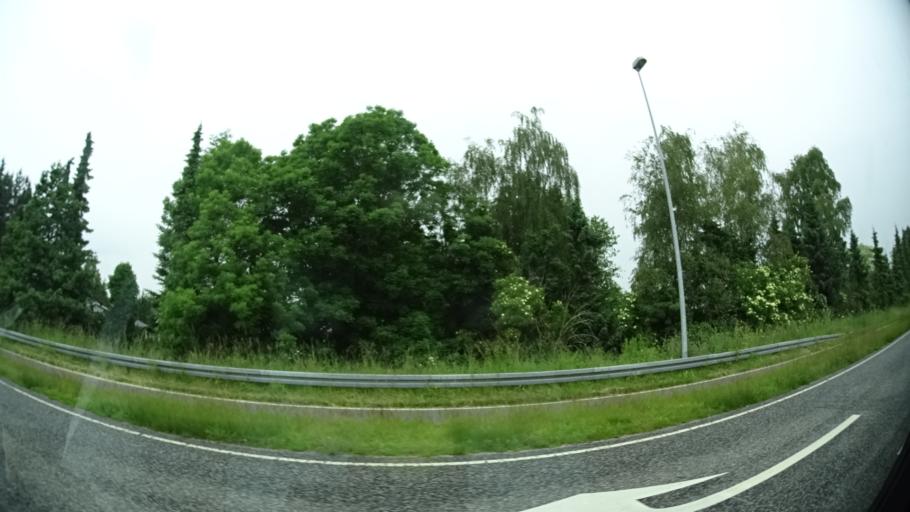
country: DK
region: Central Jutland
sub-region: Arhus Kommune
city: Hjortshoj
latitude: 56.2312
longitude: 10.2947
